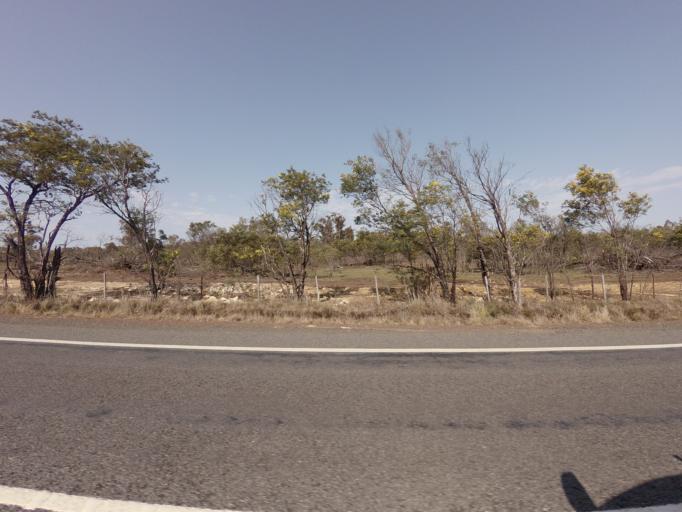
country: AU
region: Tasmania
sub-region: Northern Midlands
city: Evandale
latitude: -41.8308
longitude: 147.4867
